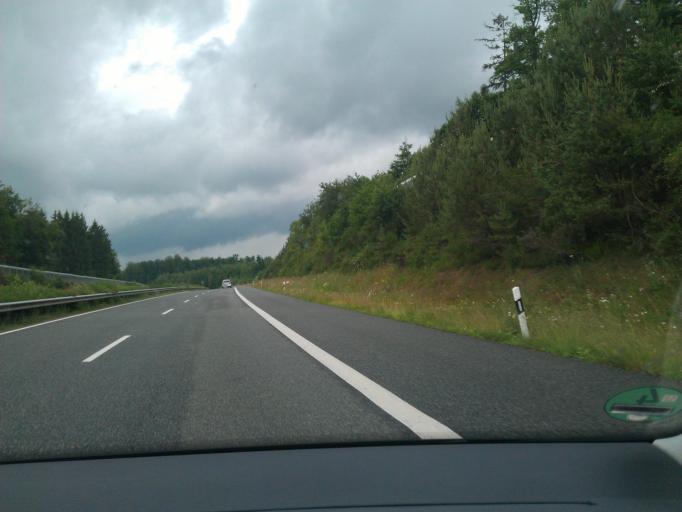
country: DE
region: Rheinland-Pfalz
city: Schwarzenborn
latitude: 50.0023
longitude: 6.7307
